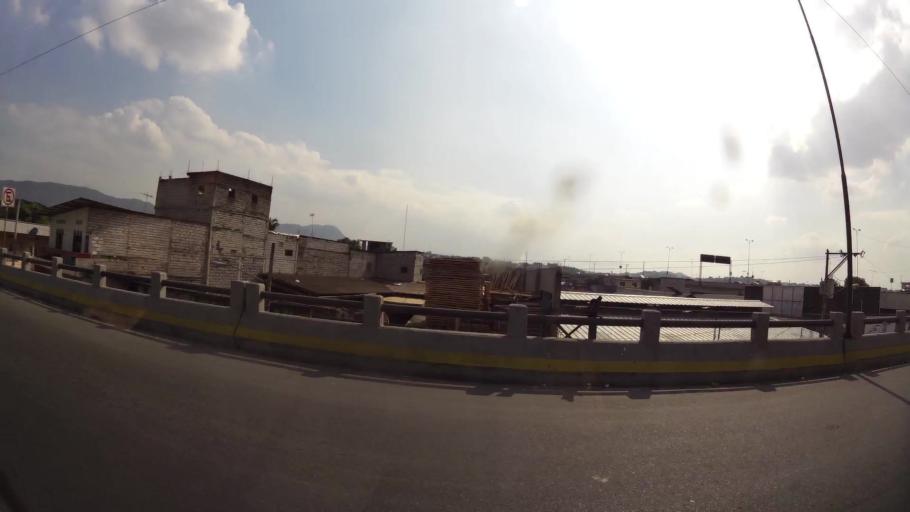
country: EC
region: Guayas
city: Guayaquil
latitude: -2.1404
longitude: -79.9353
